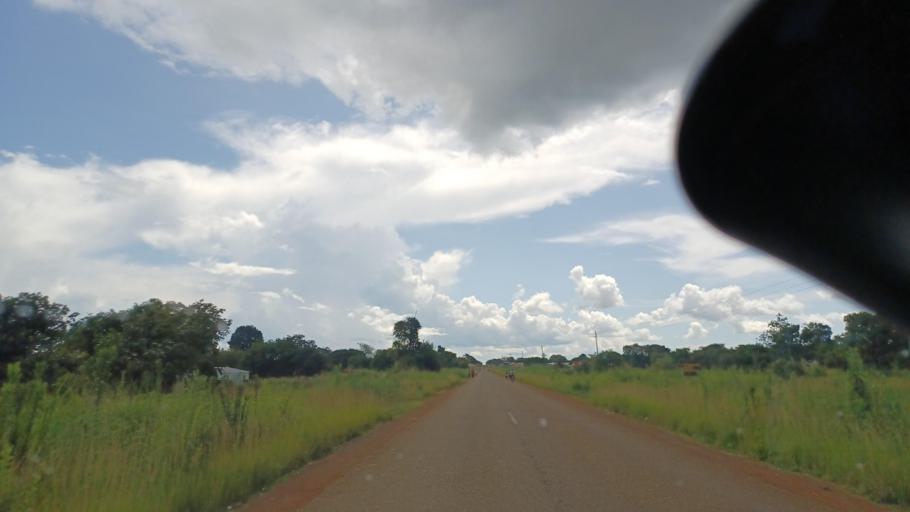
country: ZM
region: North-Western
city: Kasempa
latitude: -13.1044
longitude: 25.8762
